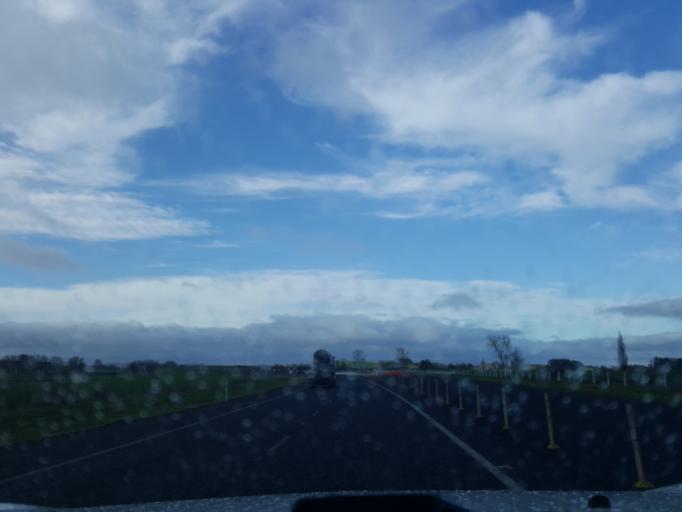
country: NZ
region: Waikato
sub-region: Waikato District
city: Ngaruawahia
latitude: -37.6743
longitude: 175.2091
